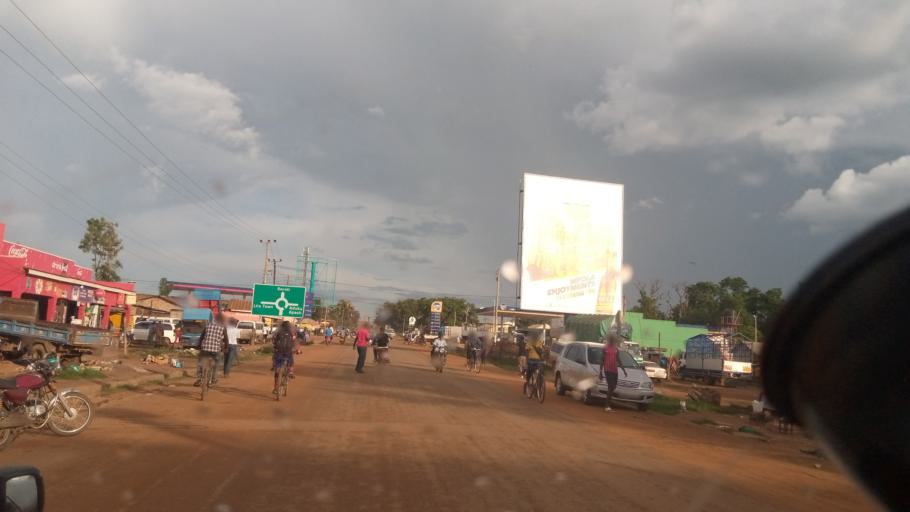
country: UG
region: Northern Region
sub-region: Lira District
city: Lira
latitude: 2.2372
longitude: 32.8909
